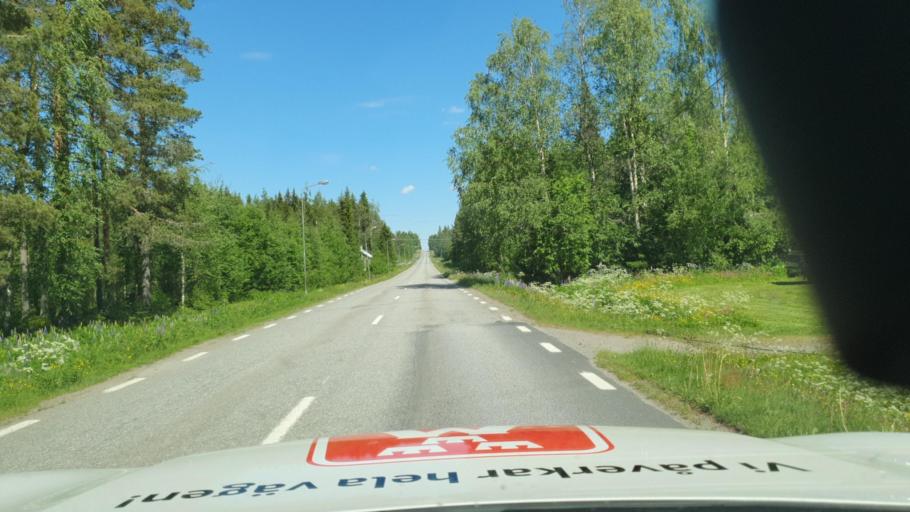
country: SE
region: Vaesterbotten
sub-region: Skelleftea Kommun
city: Boliden
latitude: 64.8522
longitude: 20.3797
